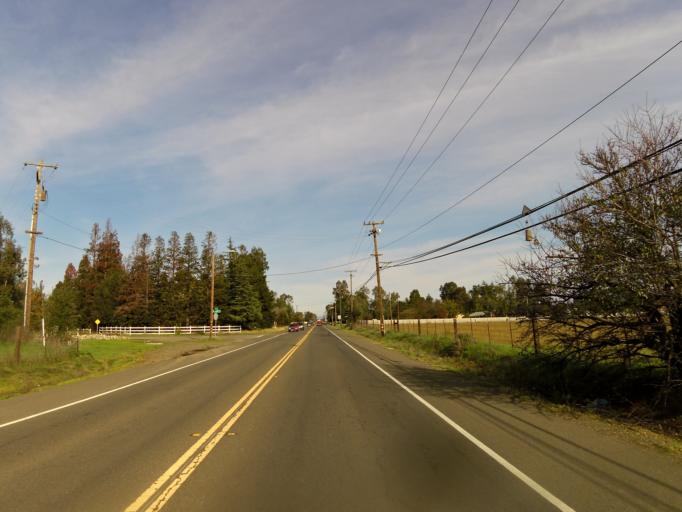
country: US
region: California
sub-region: Sacramento County
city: Wilton
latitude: 38.4416
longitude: -121.2888
